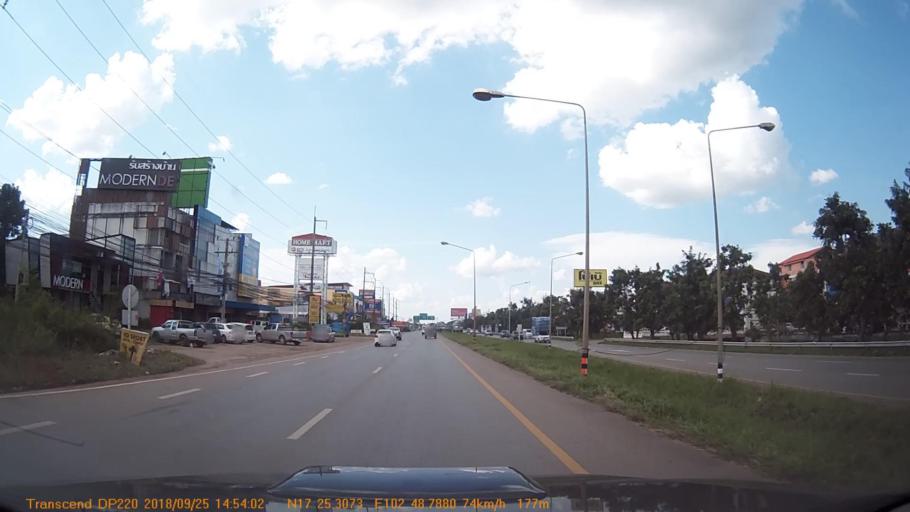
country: TH
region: Changwat Udon Thani
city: Udon Thani
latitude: 17.4222
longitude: 102.8130
